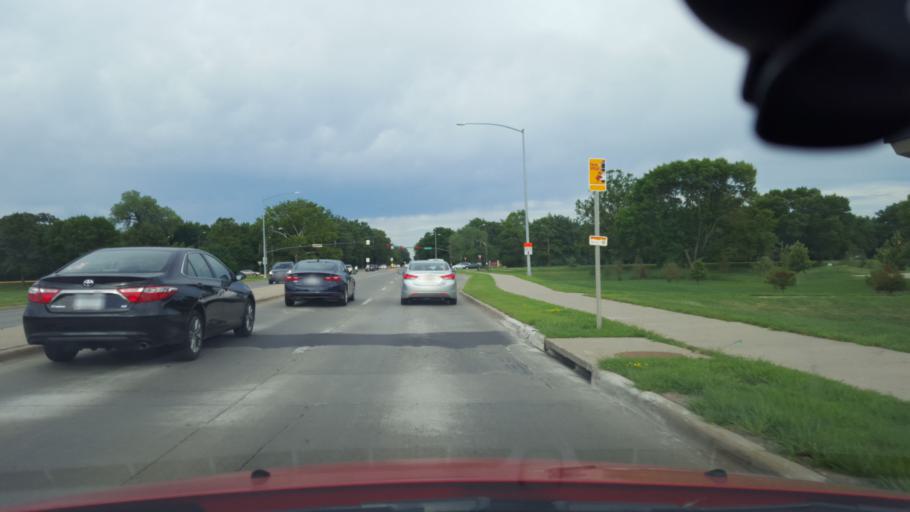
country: US
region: Iowa
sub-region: Story County
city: Ames
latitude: 42.0227
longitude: -93.6354
